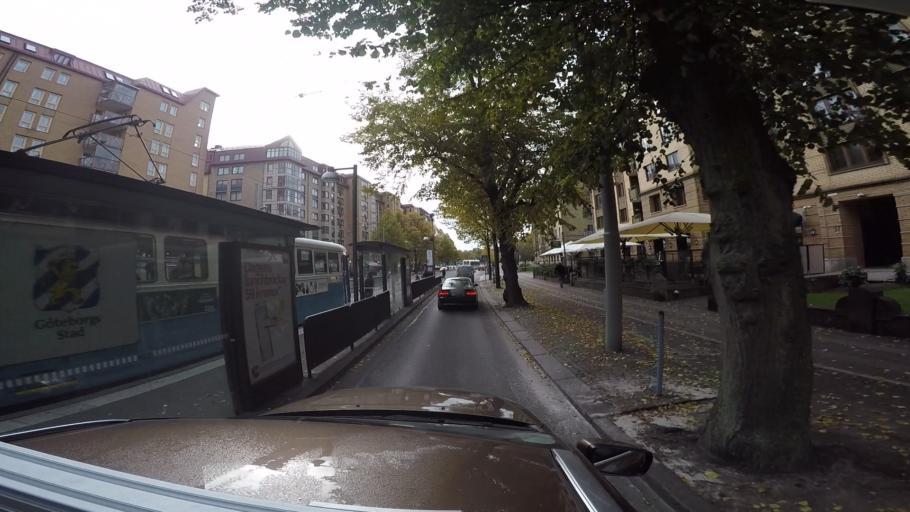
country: SE
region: Vaestra Goetaland
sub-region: Goteborg
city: Goeteborg
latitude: 57.6923
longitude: 11.9524
